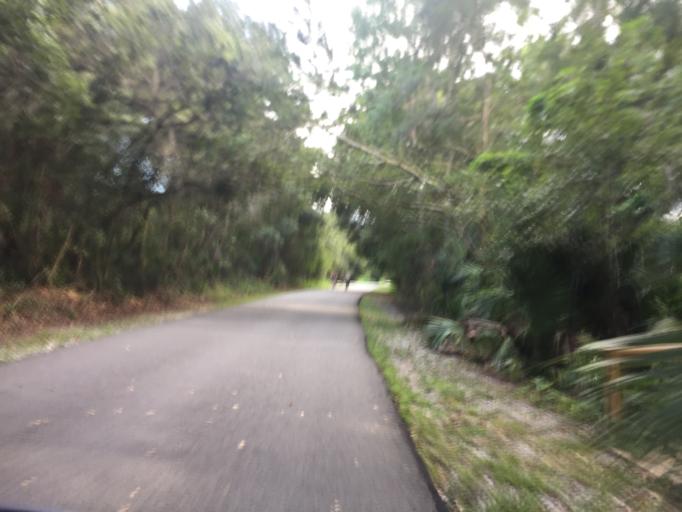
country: US
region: Florida
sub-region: Seminole County
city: Oviedo
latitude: 28.6849
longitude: -81.2312
